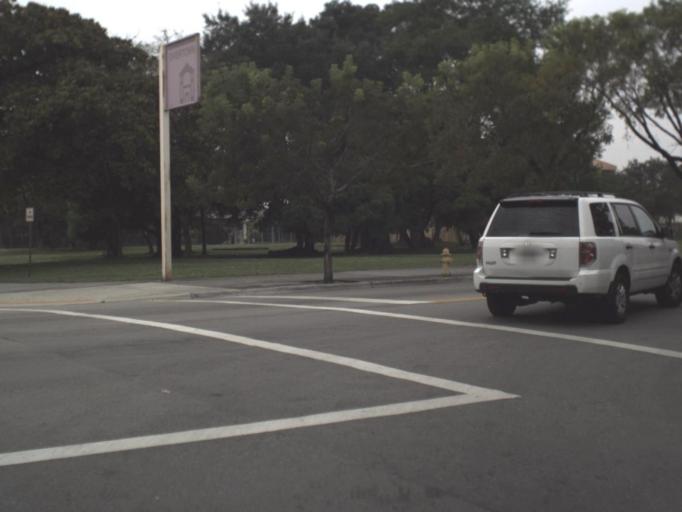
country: US
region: Florida
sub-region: Miami-Dade County
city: Miami
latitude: 25.7798
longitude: -80.1978
